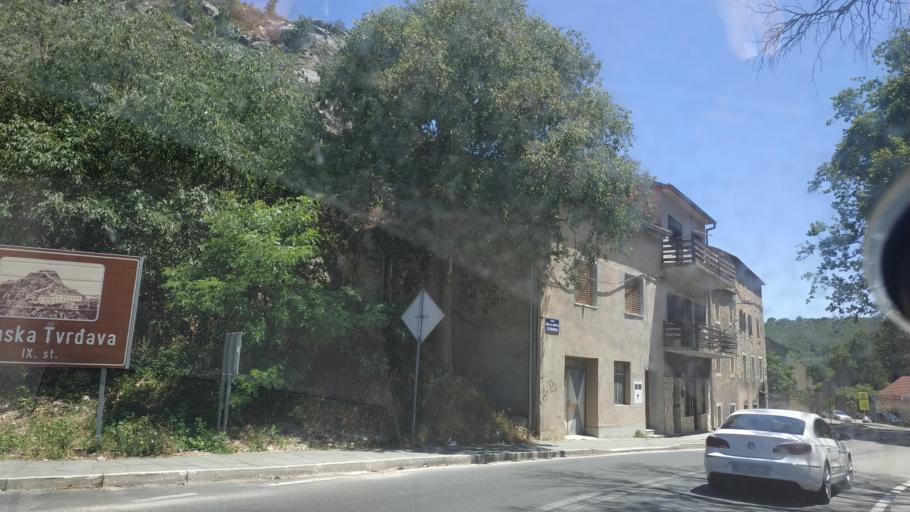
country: HR
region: Sibensko-Kniniska
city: Knin
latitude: 44.0327
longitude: 16.1906
